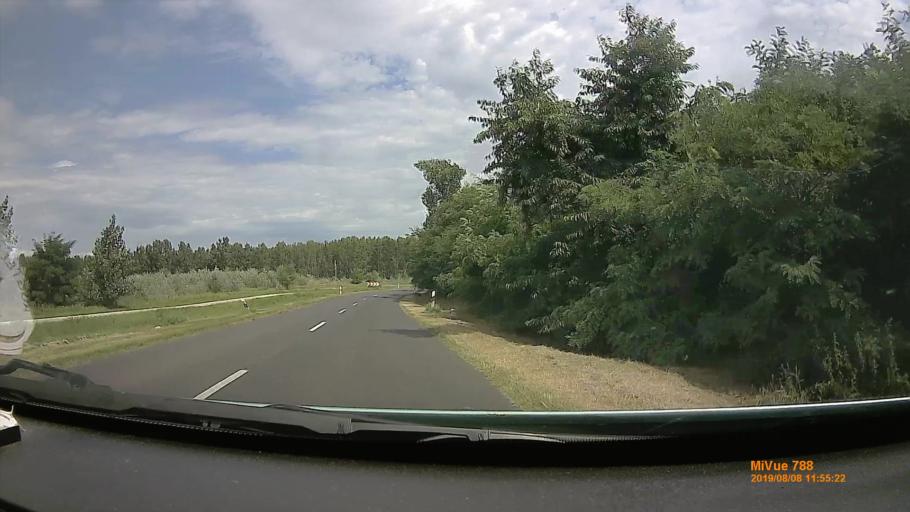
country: HU
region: Szabolcs-Szatmar-Bereg
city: Nyirmihalydi
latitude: 47.7416
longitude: 21.9787
